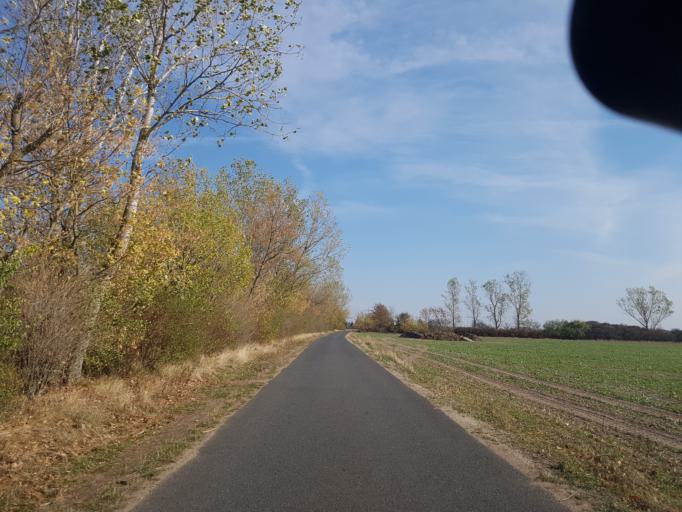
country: DE
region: Brandenburg
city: Ihlow
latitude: 51.8337
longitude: 13.3030
